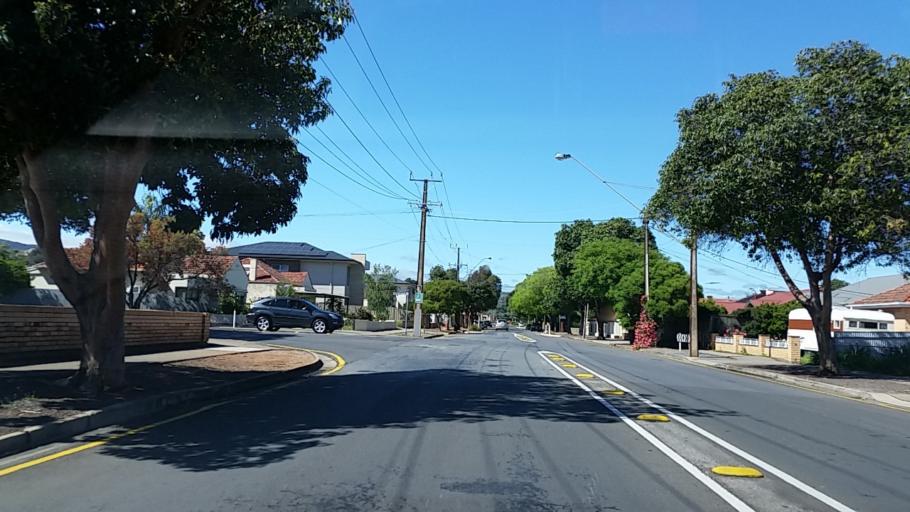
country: AU
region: South Australia
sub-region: Norwood Payneham St Peters
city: Trinity Gardens
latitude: -34.9059
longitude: 138.6506
